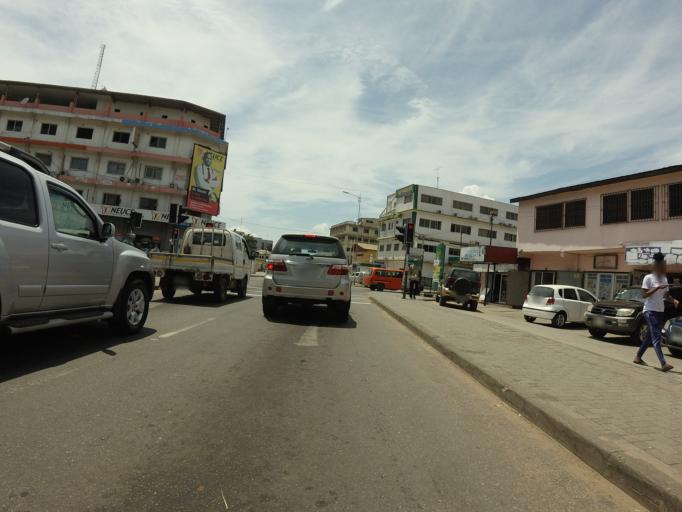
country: GH
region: Greater Accra
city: Accra
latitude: 5.5563
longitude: -0.2089
